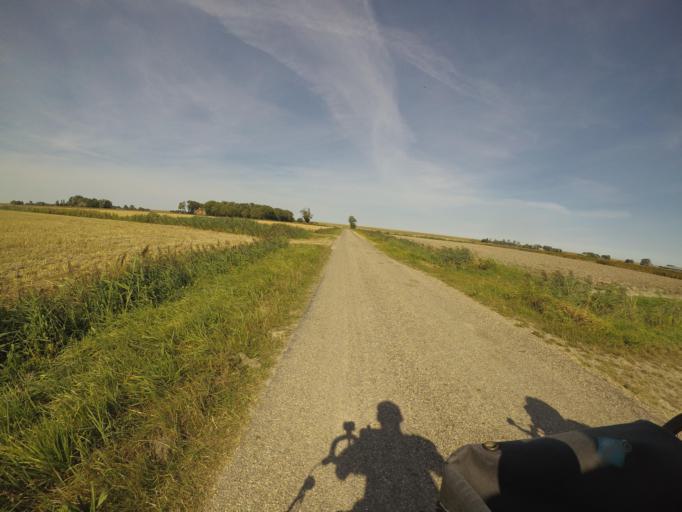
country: NL
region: Friesland
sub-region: Gemeente Ferwerderadiel
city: Ferwert
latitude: 53.3410
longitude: 5.8117
